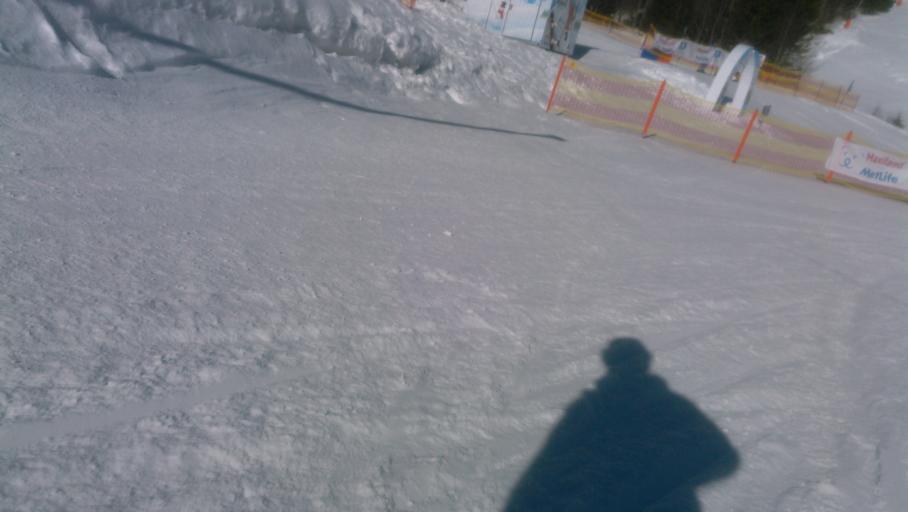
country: SK
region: Banskobystricky
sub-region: Okres Banska Bystrica
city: Brezno
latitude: 48.9224
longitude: 19.5962
